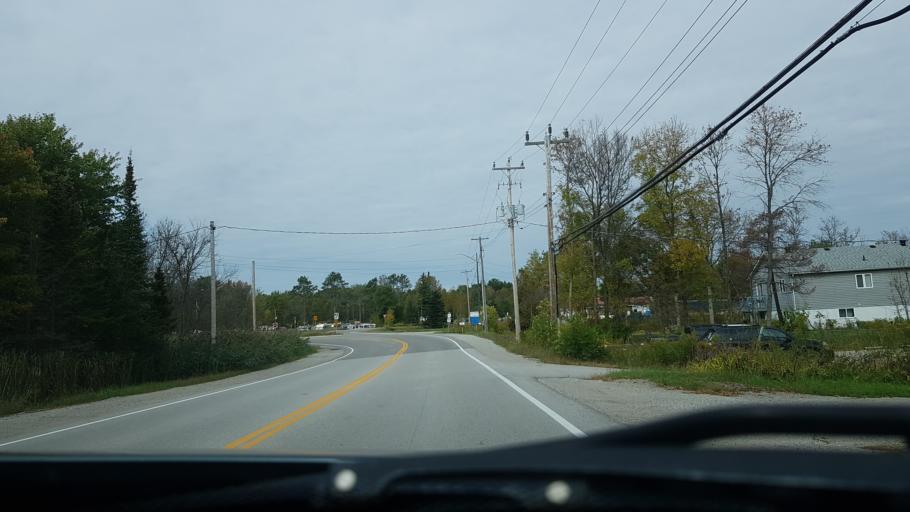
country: CA
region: Ontario
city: Gravenhurst
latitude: 44.7705
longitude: -79.3331
